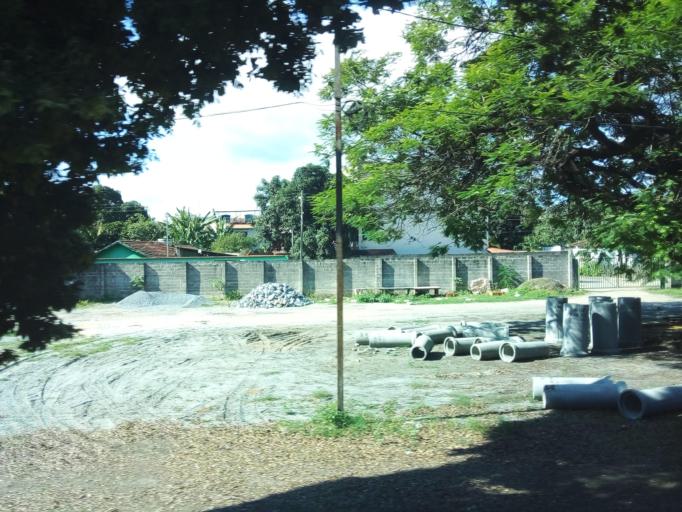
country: BR
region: Minas Gerais
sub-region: Conselheiro Pena
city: Conselheiro Pena
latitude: -18.9805
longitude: -41.6471
